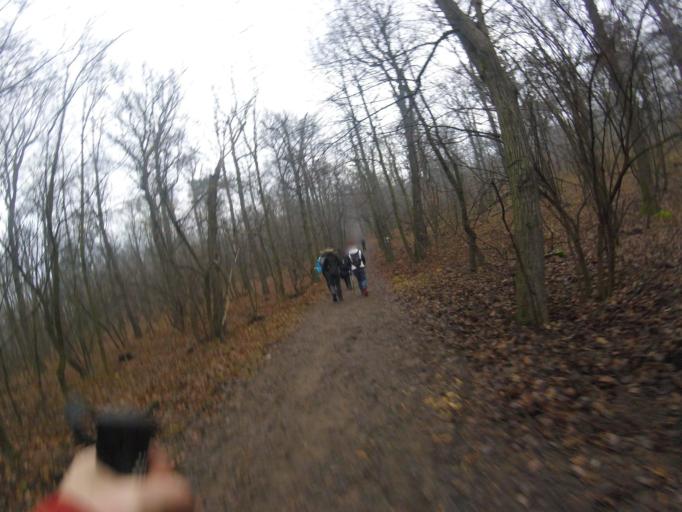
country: HU
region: Pest
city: Budakeszi
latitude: 47.5438
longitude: 18.9744
